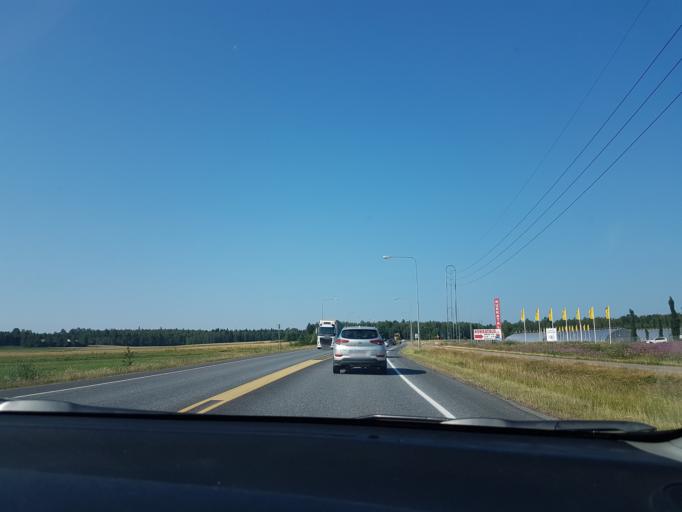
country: FI
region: Uusimaa
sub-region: Helsinki
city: Tuusula
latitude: 60.3741
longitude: 25.0471
